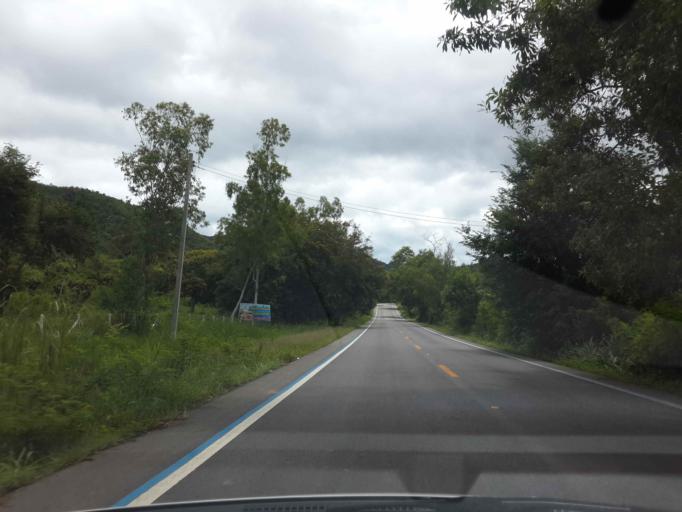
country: TH
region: Ratchaburi
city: Suan Phueng
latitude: 13.5951
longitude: 99.2382
